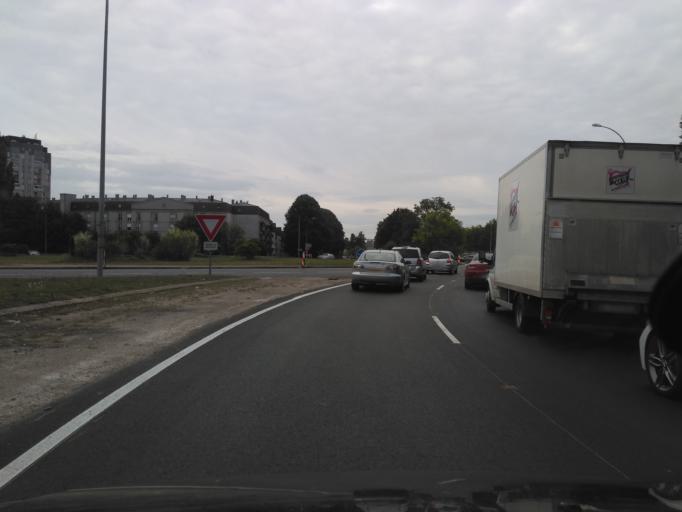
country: FR
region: Ile-de-France
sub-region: Departement de Seine-et-Marne
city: Le Mee-sur-Seine
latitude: 48.5535
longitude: 2.6428
